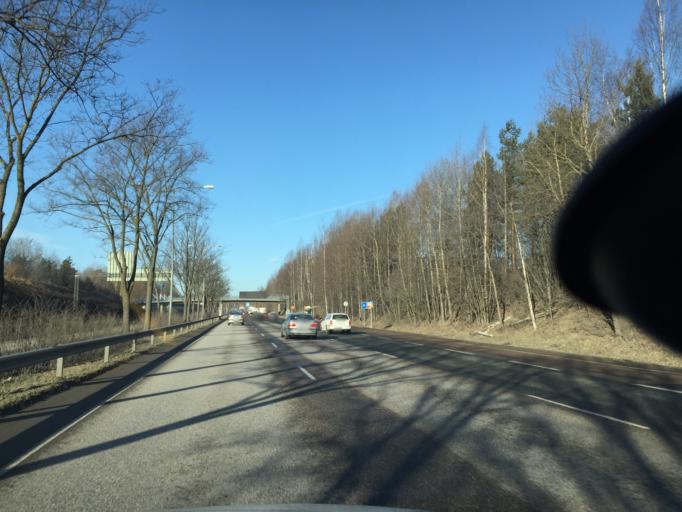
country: FI
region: Uusimaa
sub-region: Helsinki
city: Teekkarikylae
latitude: 60.2346
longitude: 24.8818
